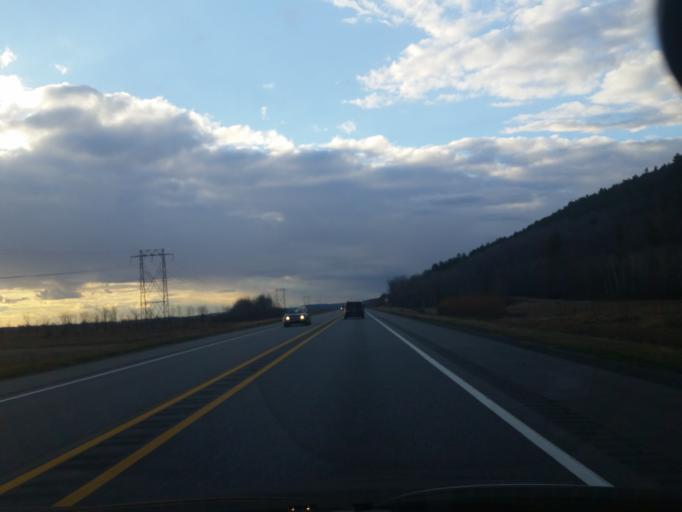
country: CA
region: Ontario
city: Hawkesbury
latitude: 45.6530
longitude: -74.8093
